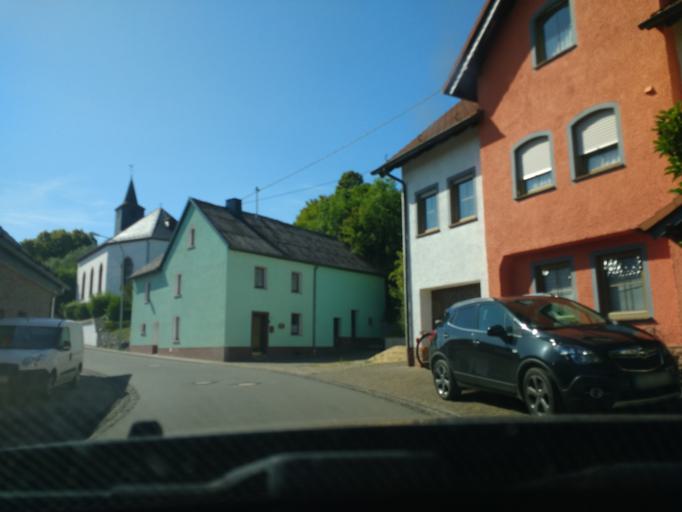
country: DE
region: Rheinland-Pfalz
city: Brockscheid
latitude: 50.1381
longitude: 6.8255
